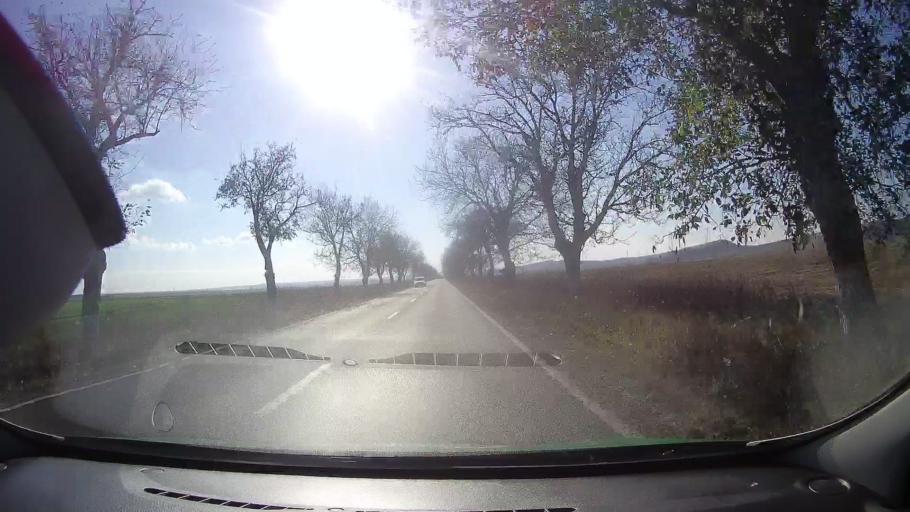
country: RO
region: Tulcea
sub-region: Comuna Ceamurlia de Jos
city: Ceamurlia de Jos
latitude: 44.7914
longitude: 28.6899
